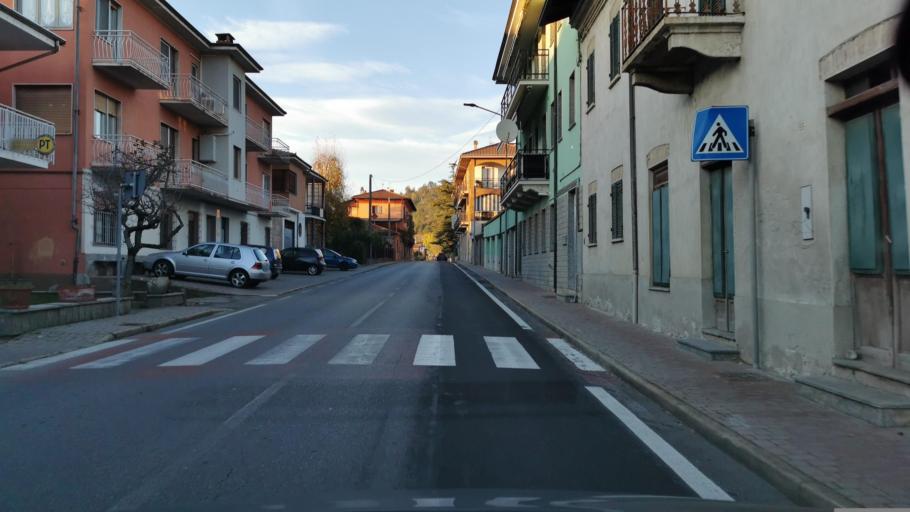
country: IT
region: Piedmont
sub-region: Provincia di Cuneo
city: Monchiero Borgonuovo
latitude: 44.5707
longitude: 7.9174
